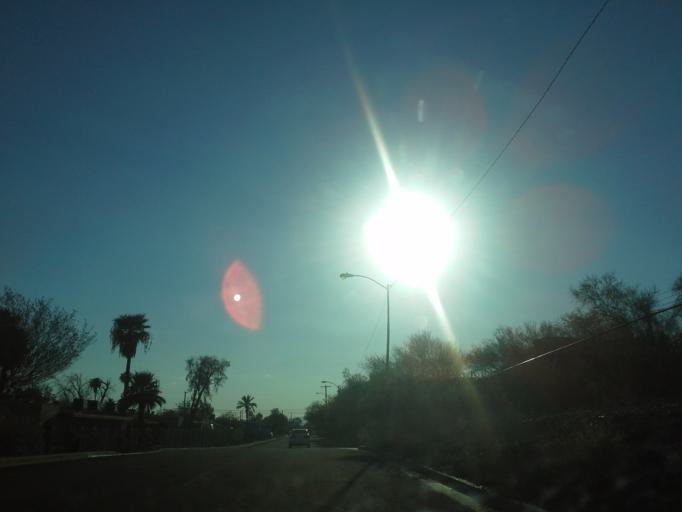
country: US
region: Arizona
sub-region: Maricopa County
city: Glendale
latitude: 33.5731
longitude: -112.0828
